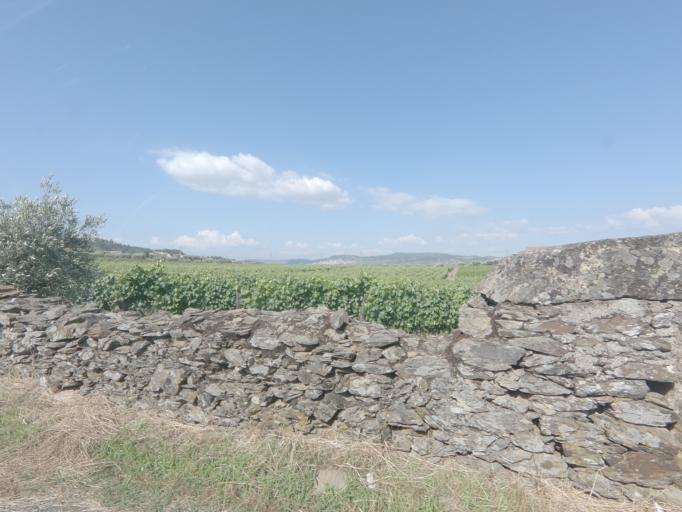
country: PT
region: Vila Real
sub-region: Sabrosa
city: Sabrosa
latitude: 41.2605
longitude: -7.5776
